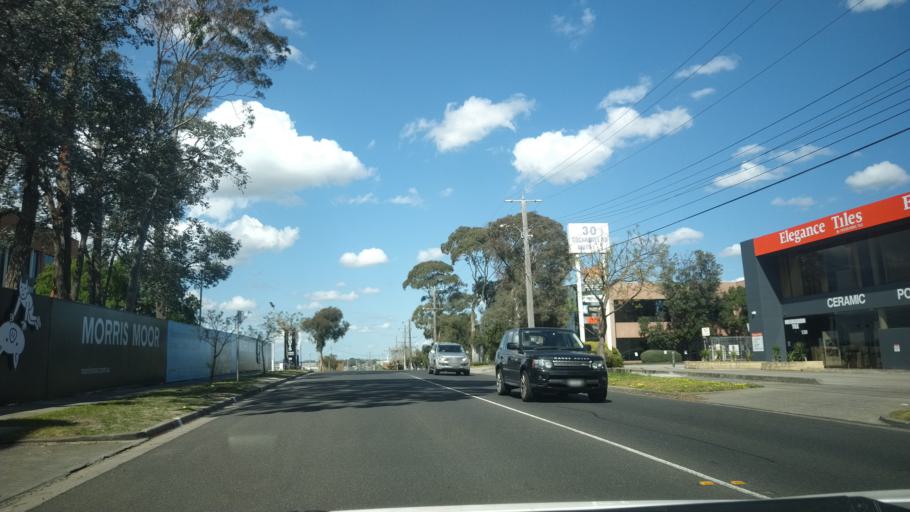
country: AU
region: Victoria
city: Highett
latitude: -37.9423
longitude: 145.0633
